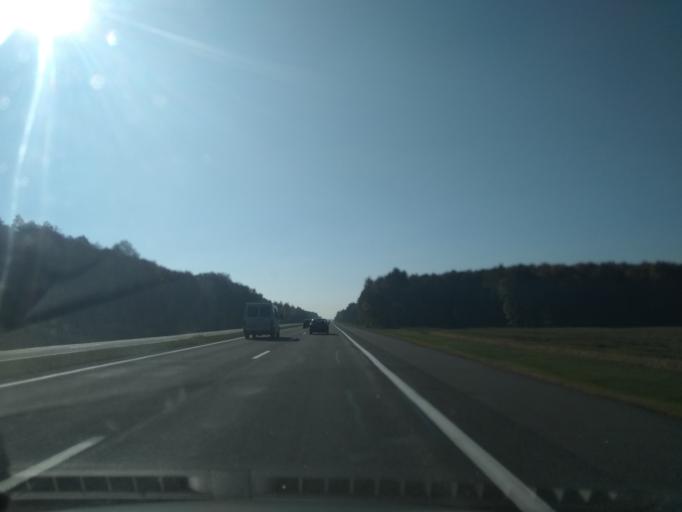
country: BY
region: Brest
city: Ivatsevichy
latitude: 52.8090
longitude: 25.5757
